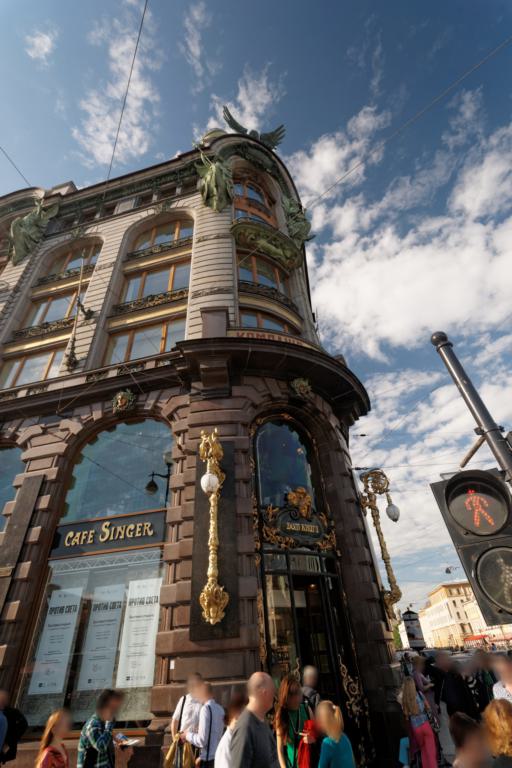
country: RU
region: St.-Petersburg
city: Saint Petersburg
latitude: 59.9355
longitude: 30.3260
